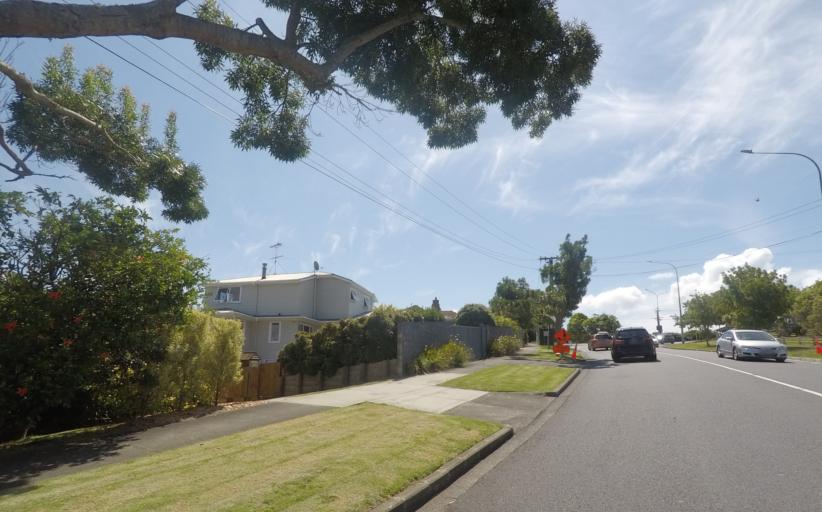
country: NZ
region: Auckland
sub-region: Auckland
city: Tamaki
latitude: -36.8686
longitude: 174.8489
